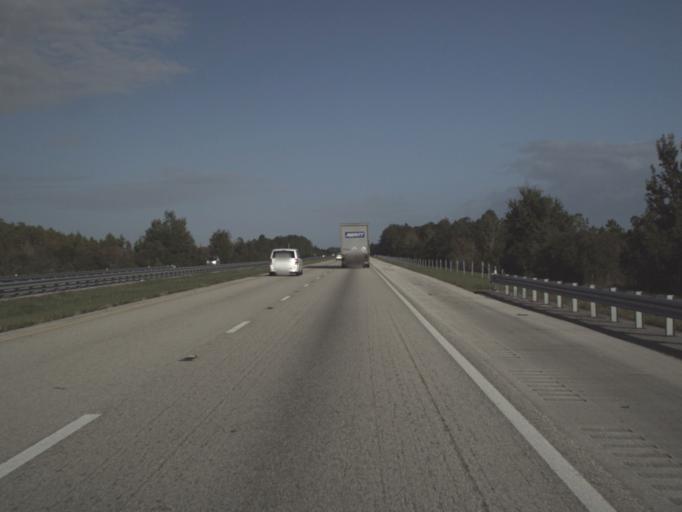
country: US
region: Florida
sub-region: Brevard County
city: June Park
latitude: 27.8956
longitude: -81.0398
